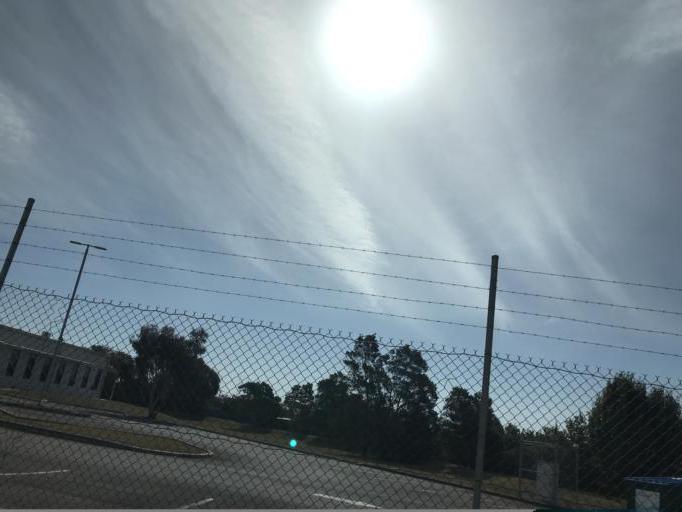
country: AU
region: Victoria
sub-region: Ballarat North
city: Newington
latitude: -37.5337
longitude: 143.8210
